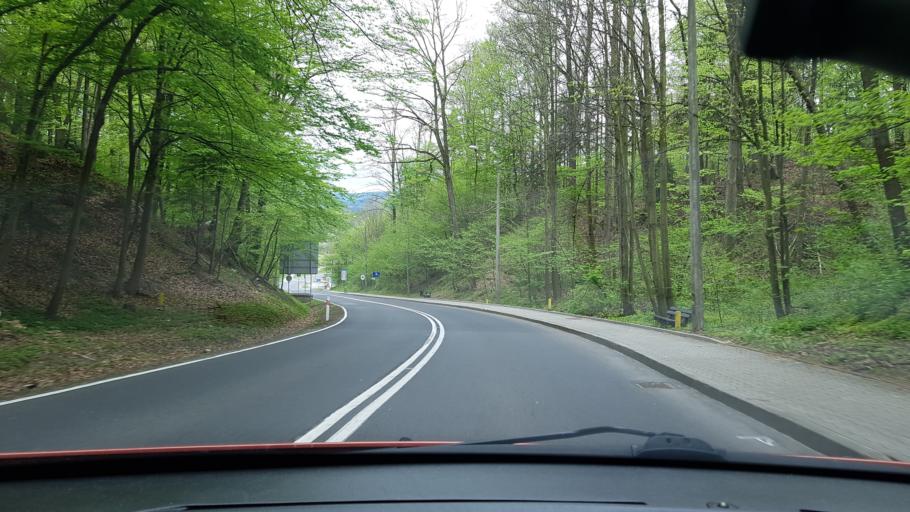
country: CZ
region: Olomoucky
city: Mikulovice
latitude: 50.3119
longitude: 17.3508
